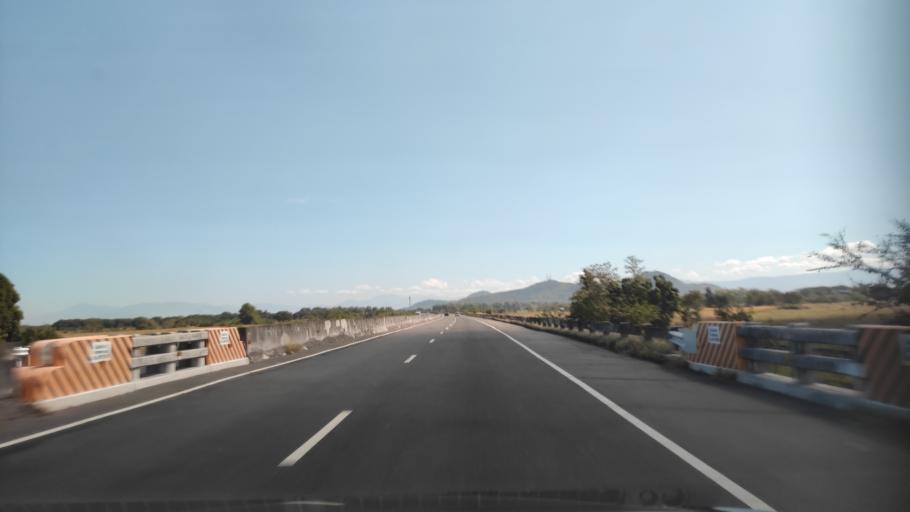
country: PH
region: Central Luzon
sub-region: Province of Nueva Ecija
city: Nampicuan
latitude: 15.7624
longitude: 120.6370
